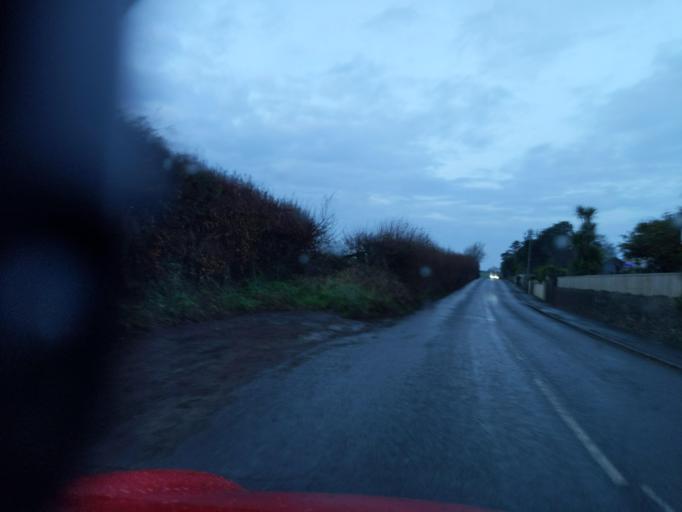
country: GB
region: England
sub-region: Devon
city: Wembury
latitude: 50.3378
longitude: -4.0733
